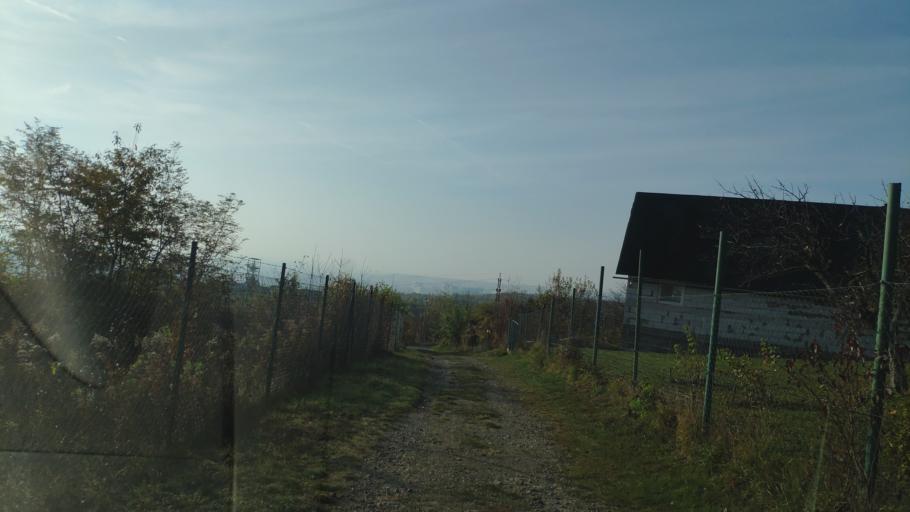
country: SK
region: Kosicky
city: Kosice
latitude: 48.7438
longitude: 21.2198
